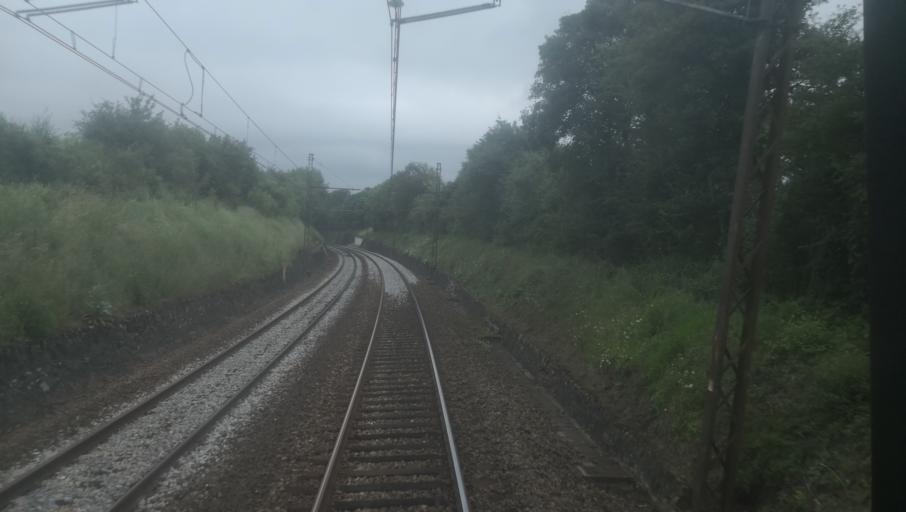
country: FR
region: Centre
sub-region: Departement de l'Indre
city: Le Pechereau
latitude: 46.5283
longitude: 1.5291
